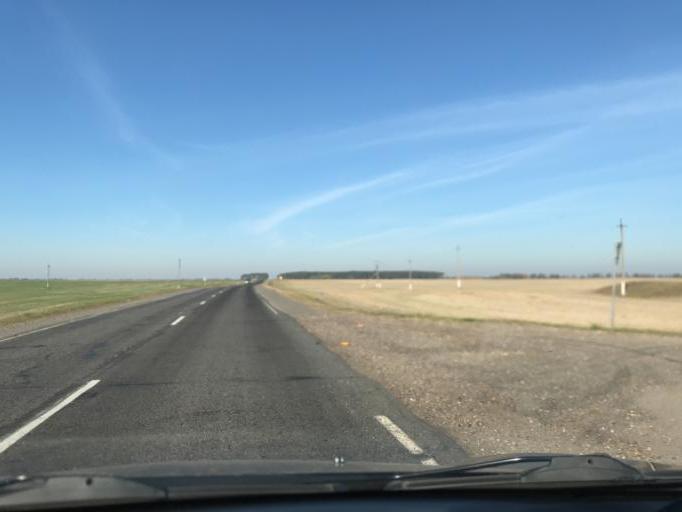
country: BY
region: Gomel
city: Brahin
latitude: 51.8026
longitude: 30.1232
